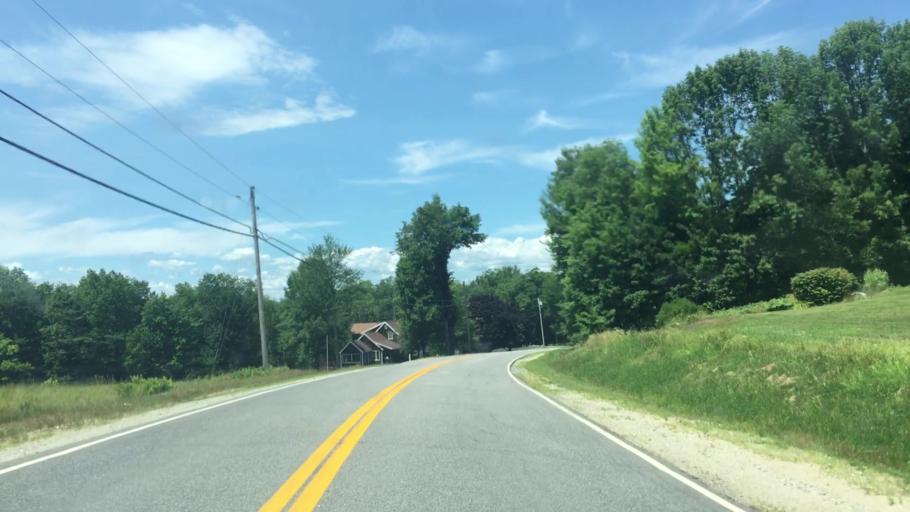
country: US
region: Maine
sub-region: Androscoggin County
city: Livermore
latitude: 44.3847
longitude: -70.2120
